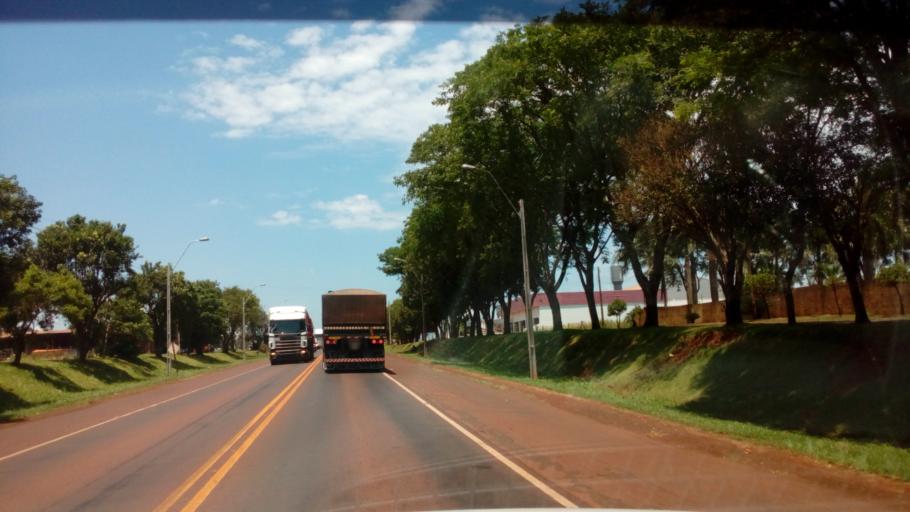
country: PY
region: Alto Parana
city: Santa Rita
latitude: -25.8160
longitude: -55.1080
